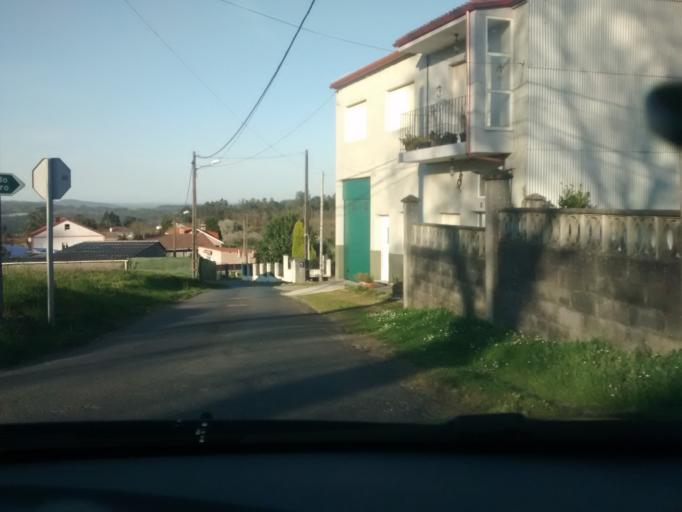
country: ES
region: Galicia
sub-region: Provincia de Pontevedra
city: A Estrada
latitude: 42.6943
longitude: -8.4832
